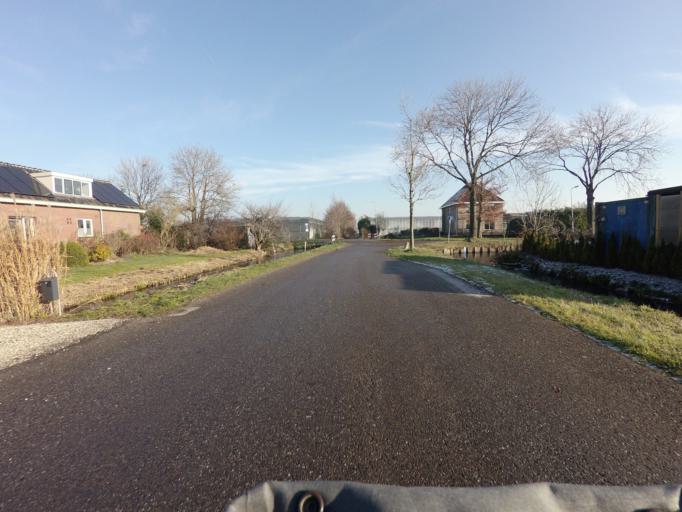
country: NL
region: Utrecht
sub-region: Gemeente De Ronde Venen
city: Mijdrecht
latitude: 52.1727
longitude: 4.8590
